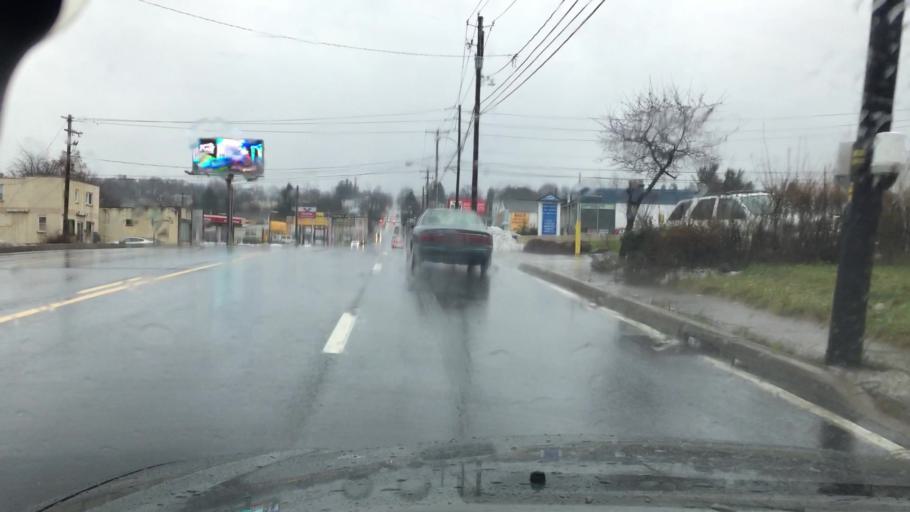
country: US
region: Pennsylvania
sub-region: Luzerne County
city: Harleigh
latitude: 40.9752
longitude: -75.9787
